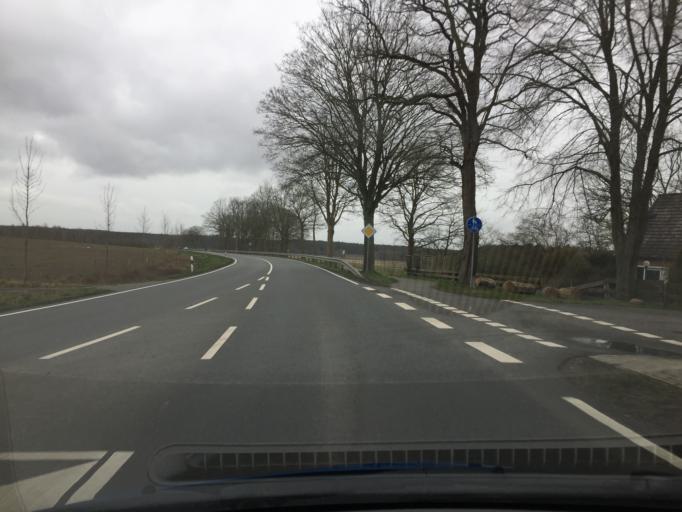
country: DE
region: Lower Saxony
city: Stoetze
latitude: 53.0532
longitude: 10.8145
